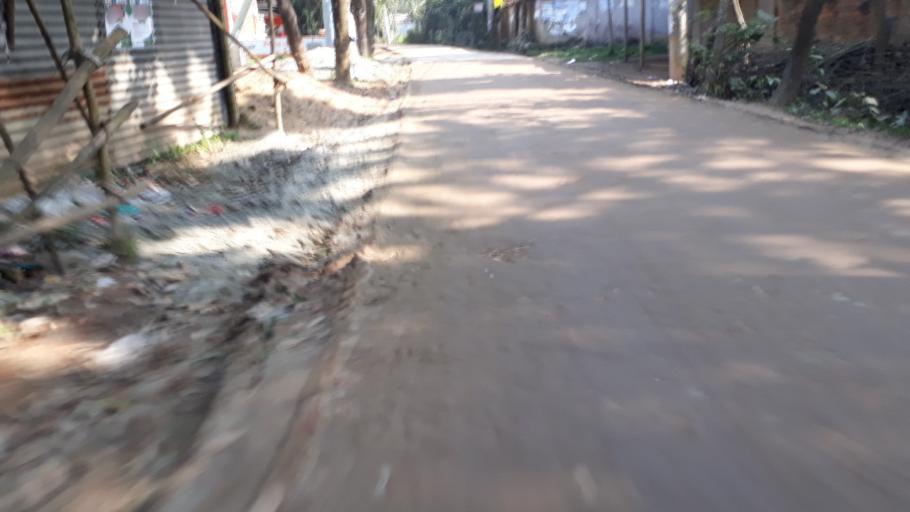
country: BD
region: Dhaka
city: Tungi
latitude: 23.8544
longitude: 90.3018
